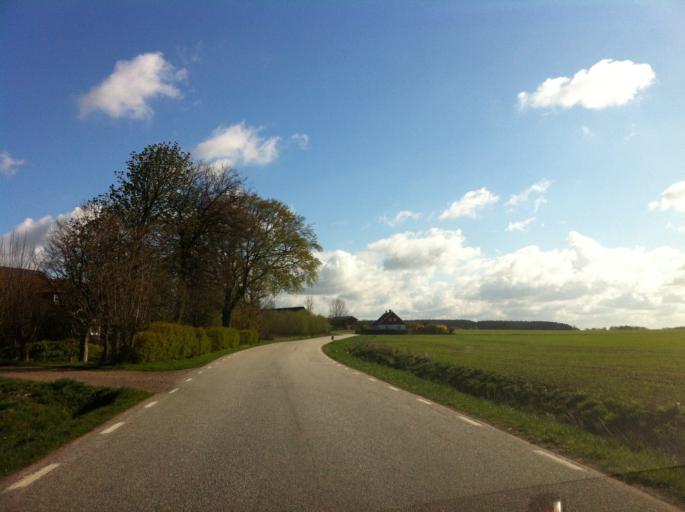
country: SE
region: Skane
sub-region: Eslovs Kommun
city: Eslov
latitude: 55.8668
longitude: 13.2440
